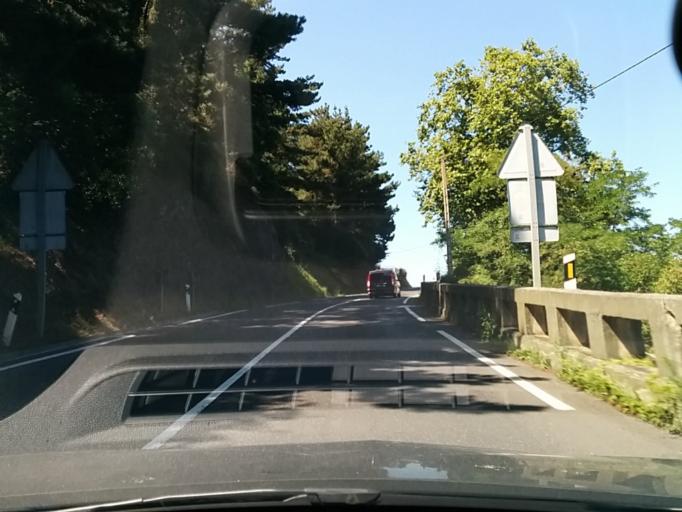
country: ES
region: Basque Country
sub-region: Bizkaia
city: Ondarroa
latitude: 43.3191
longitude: -2.4132
